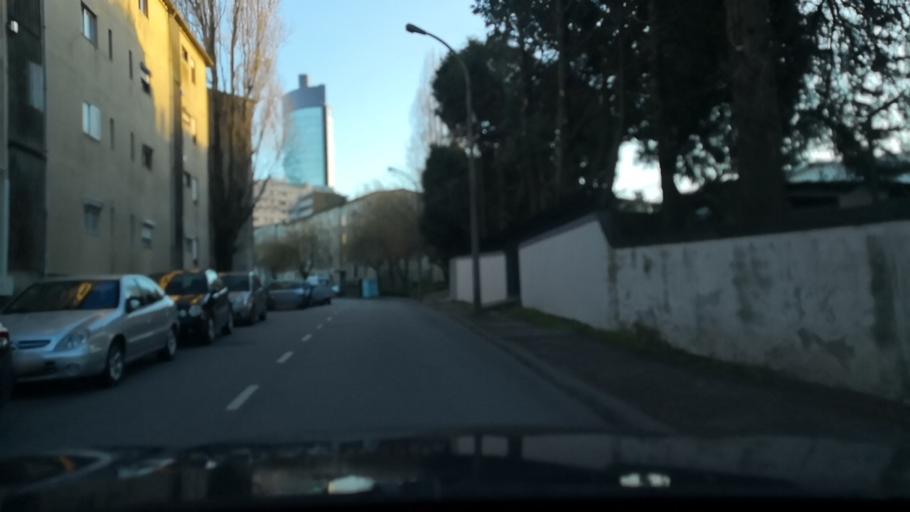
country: PT
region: Porto
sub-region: Maia
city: Maia
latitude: 41.2362
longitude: -8.6208
